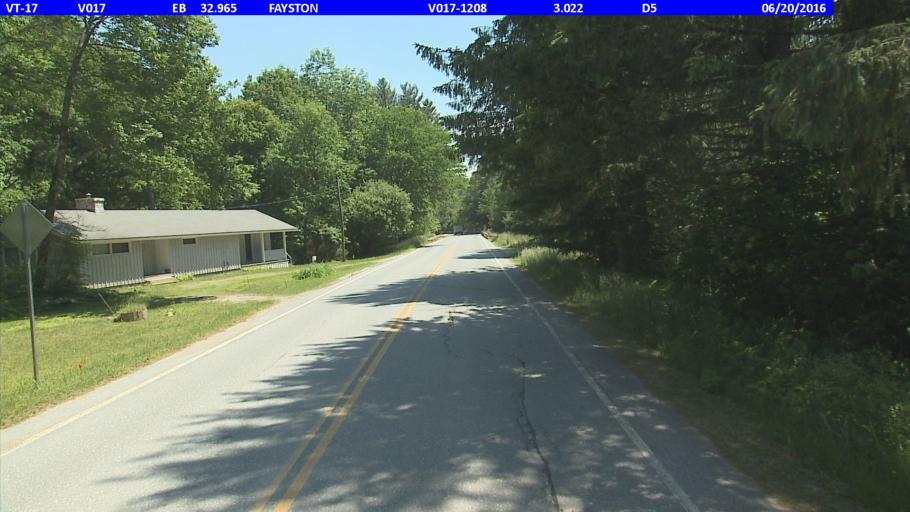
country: US
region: Vermont
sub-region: Washington County
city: Waterbury
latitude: 44.1951
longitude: -72.8907
